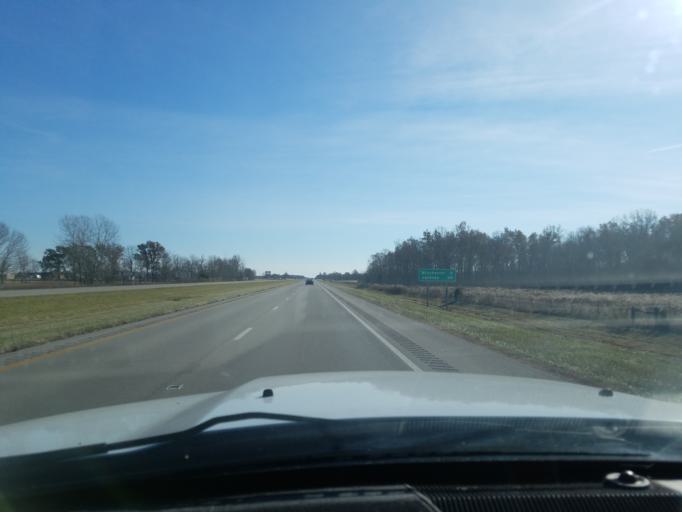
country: US
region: Ohio
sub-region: Adams County
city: Winchester
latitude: 38.9660
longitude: -83.7250
